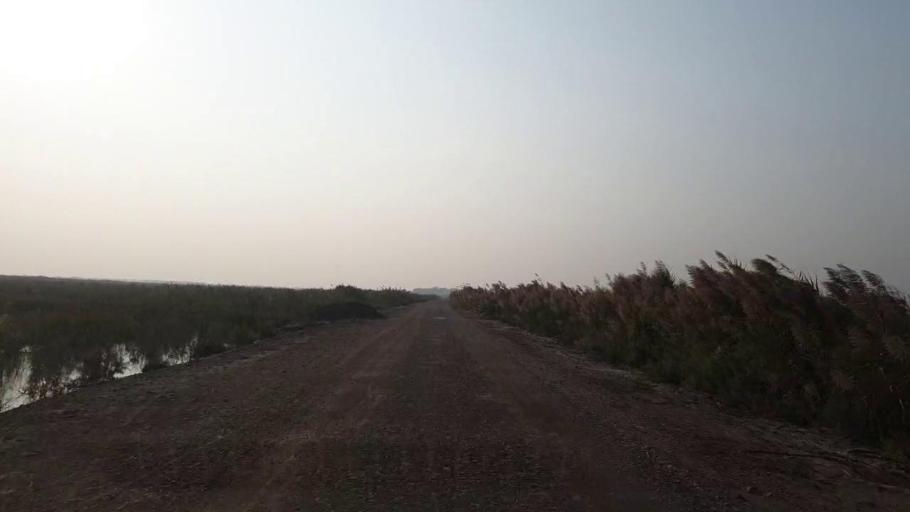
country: PK
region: Sindh
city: Bulri
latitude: 25.0853
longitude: 68.3190
